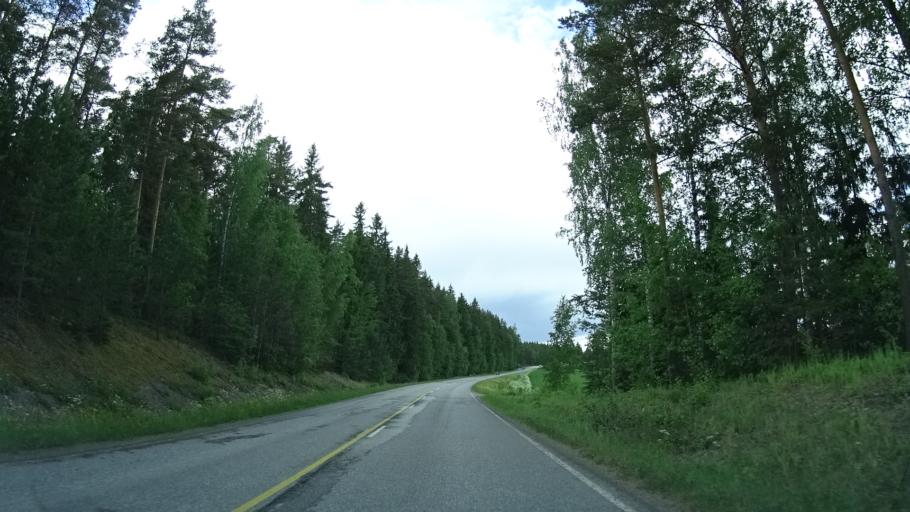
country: FI
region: Paijanne Tavastia
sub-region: Lahti
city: Sysmae
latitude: 61.3843
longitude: 25.6504
